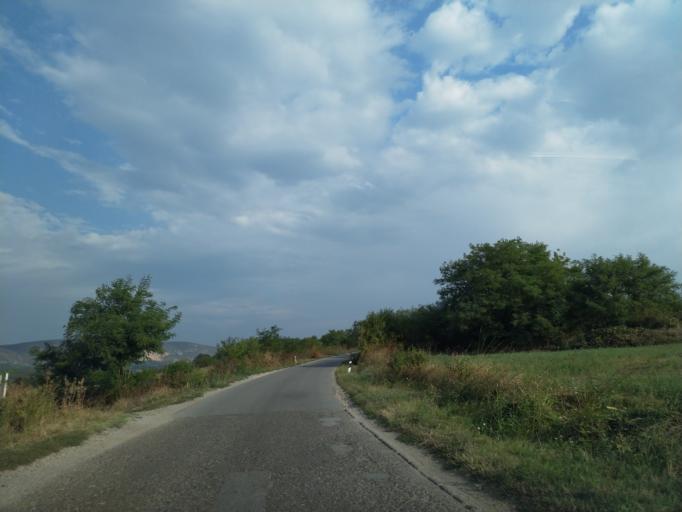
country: RS
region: Central Serbia
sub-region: Pomoravski Okrug
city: Paracin
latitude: 43.8426
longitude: 21.4895
